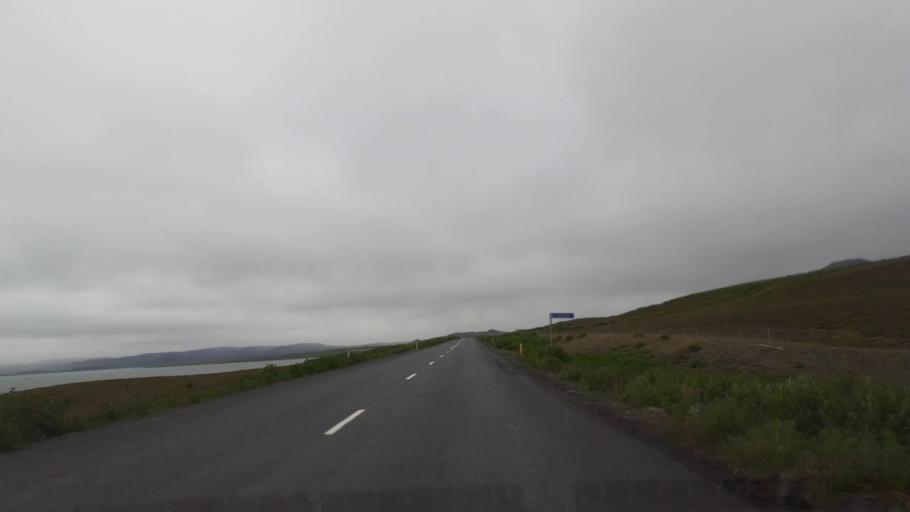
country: IS
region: Northeast
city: Husavik
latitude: 66.2213
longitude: -16.4568
